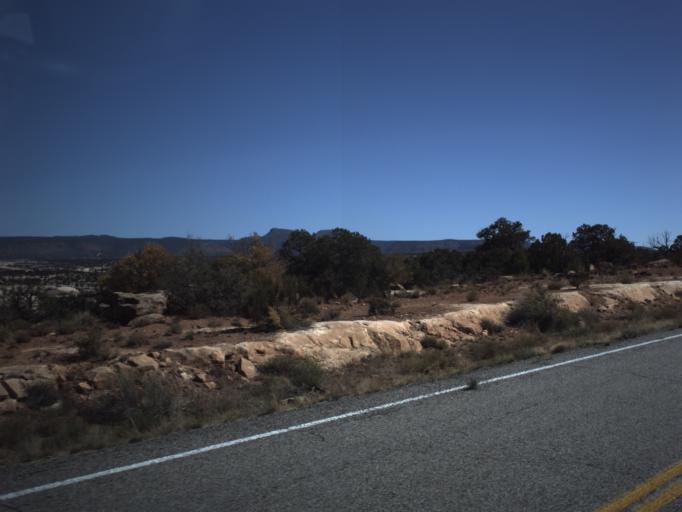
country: US
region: Utah
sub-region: San Juan County
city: Blanding
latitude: 37.5974
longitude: -110.0497
